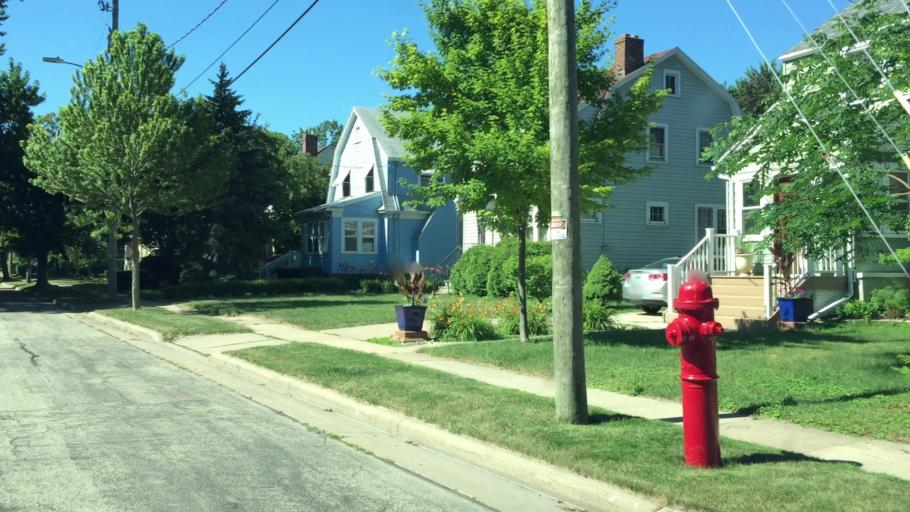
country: US
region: Wisconsin
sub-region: Winnebago County
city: Menasha
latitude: 44.1994
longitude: -88.4432
